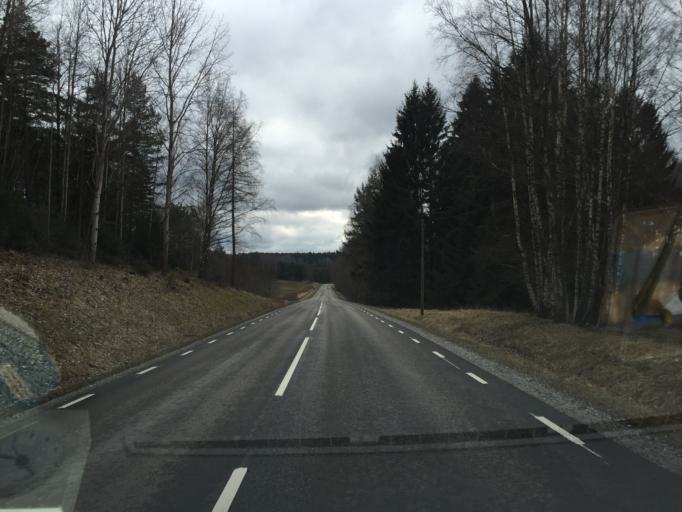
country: SE
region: Stockholm
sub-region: Botkyrka Kommun
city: Eriksberg
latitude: 59.2213
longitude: 17.7812
